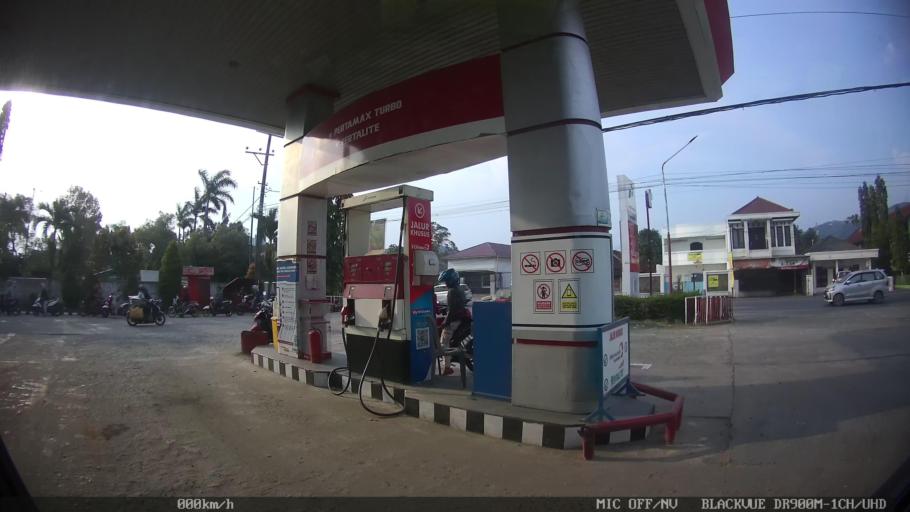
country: ID
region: Lampung
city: Panjang
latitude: -5.4451
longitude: 105.2940
